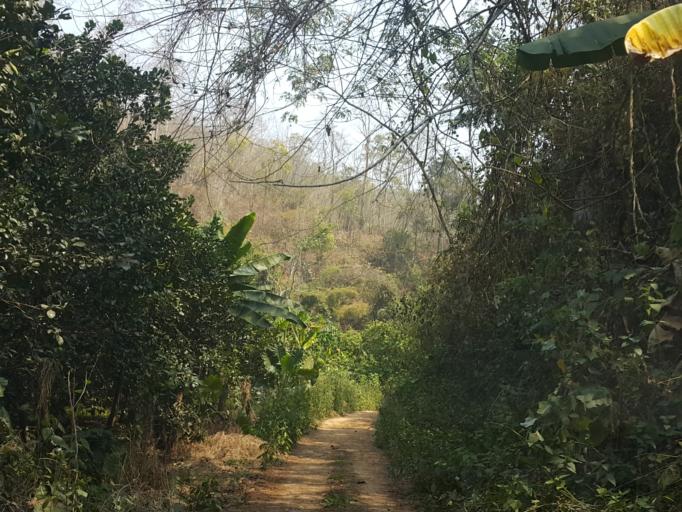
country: TH
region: Chiang Mai
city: Hang Dong
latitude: 18.7569
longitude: 98.8237
